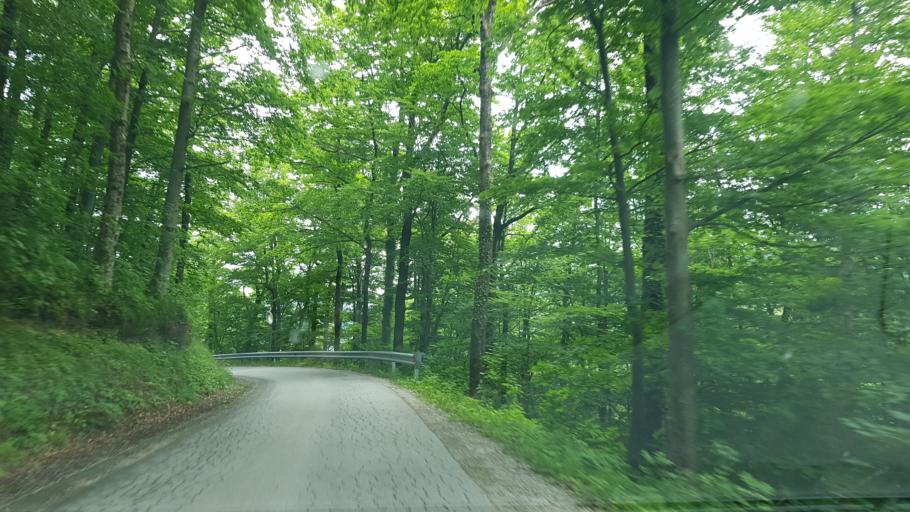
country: SI
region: Dobrna
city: Dobrna
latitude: 46.3530
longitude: 15.2380
